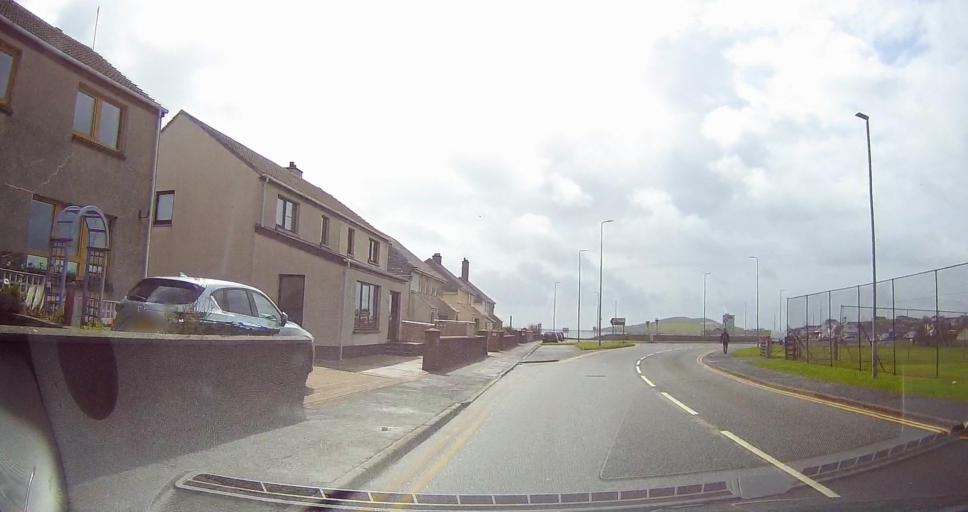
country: GB
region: Scotland
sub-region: Shetland Islands
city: Lerwick
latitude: 60.1508
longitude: -1.1599
